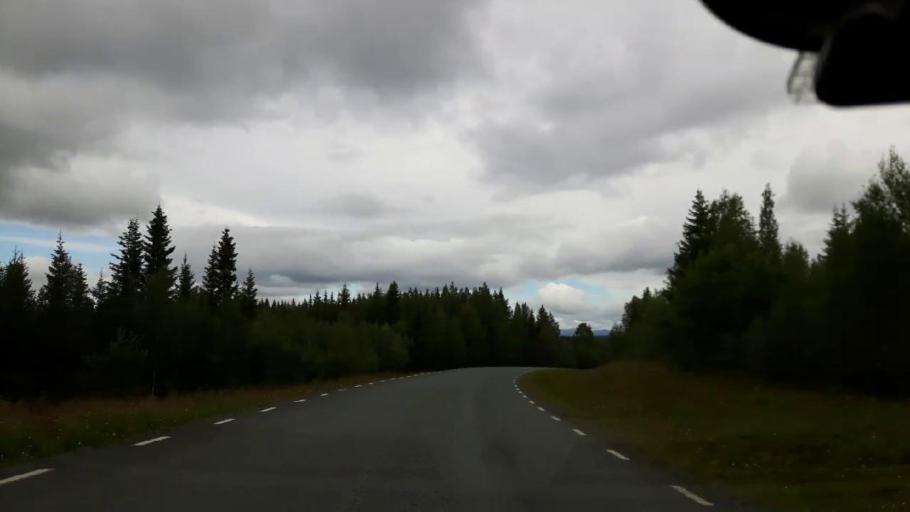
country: SE
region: Jaemtland
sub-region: Krokoms Kommun
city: Valla
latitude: 63.5482
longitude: 13.8504
